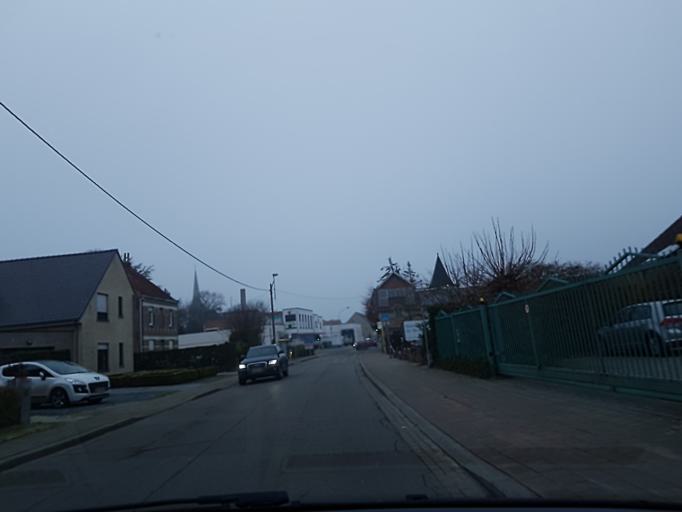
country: BE
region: Flanders
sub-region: Provincie Vlaams-Brabant
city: Kapelle-op-den-Bos
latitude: 50.9778
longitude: 4.3533
